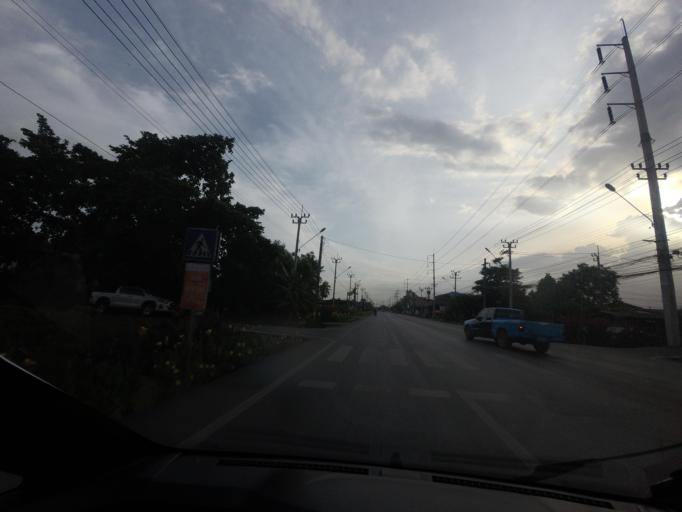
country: TH
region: Bangkok
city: Nong Chok
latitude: 13.8523
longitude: 100.8023
